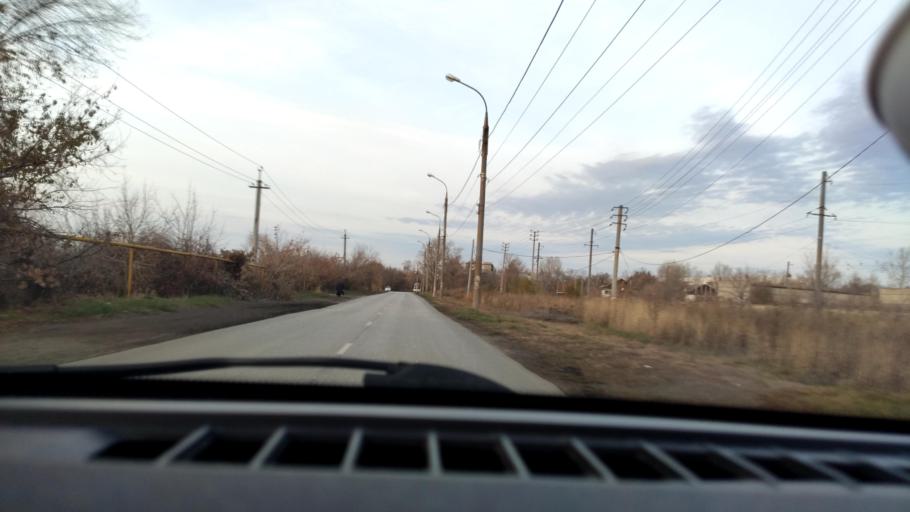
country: RU
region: Samara
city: Samara
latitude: 53.1458
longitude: 50.1343
